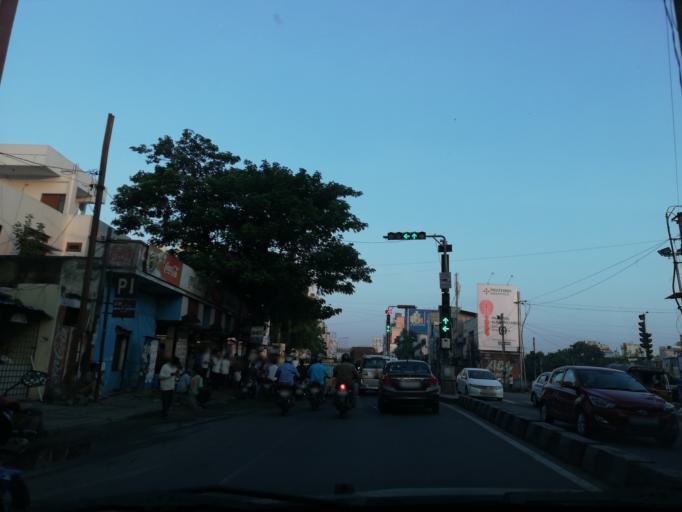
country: IN
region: Telangana
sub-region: Rangareddi
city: Gaddi Annaram
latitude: 17.3961
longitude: 78.4968
